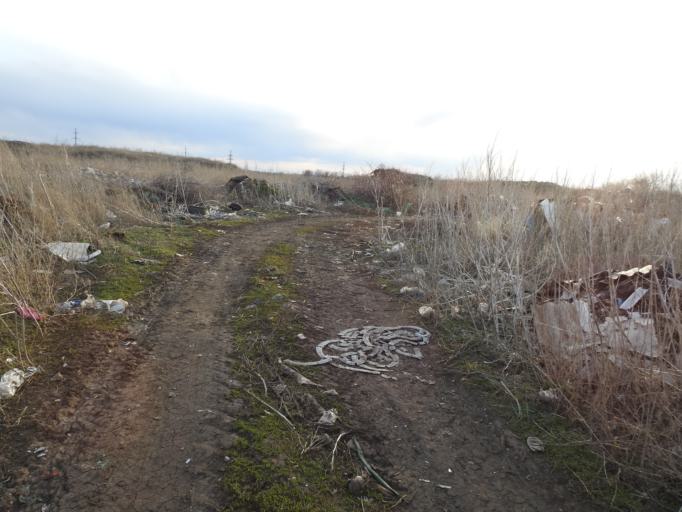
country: RU
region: Saratov
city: Engel's
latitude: 51.4228
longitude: 46.1820
